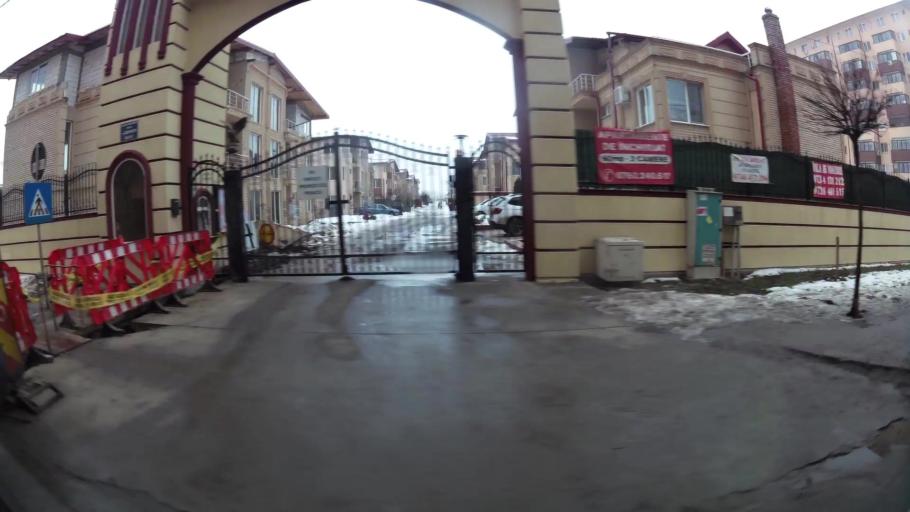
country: RO
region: Ilfov
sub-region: Comuna Chiajna
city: Chiajna
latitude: 44.4457
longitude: 25.9874
